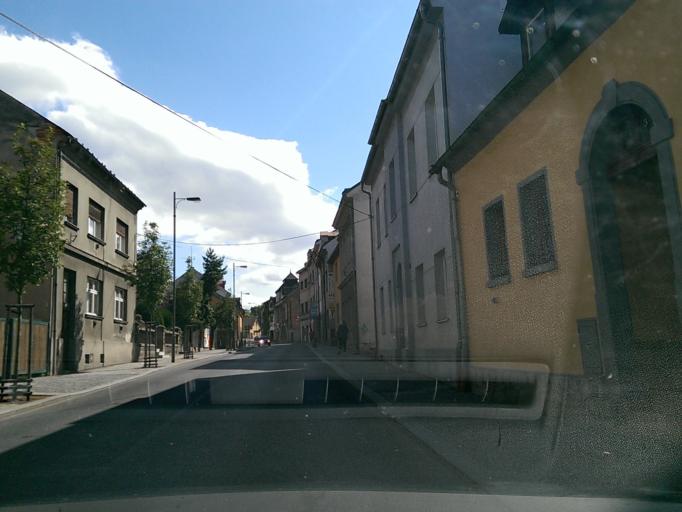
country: CZ
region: Liberecky
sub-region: Okres Semily
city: Turnov
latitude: 50.5884
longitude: 15.1602
